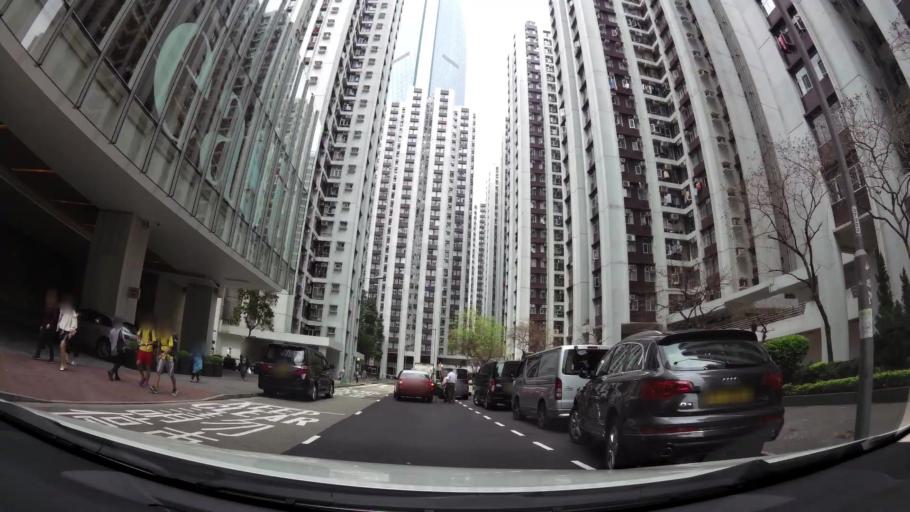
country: HK
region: Wanchai
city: Wan Chai
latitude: 22.2860
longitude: 114.2161
